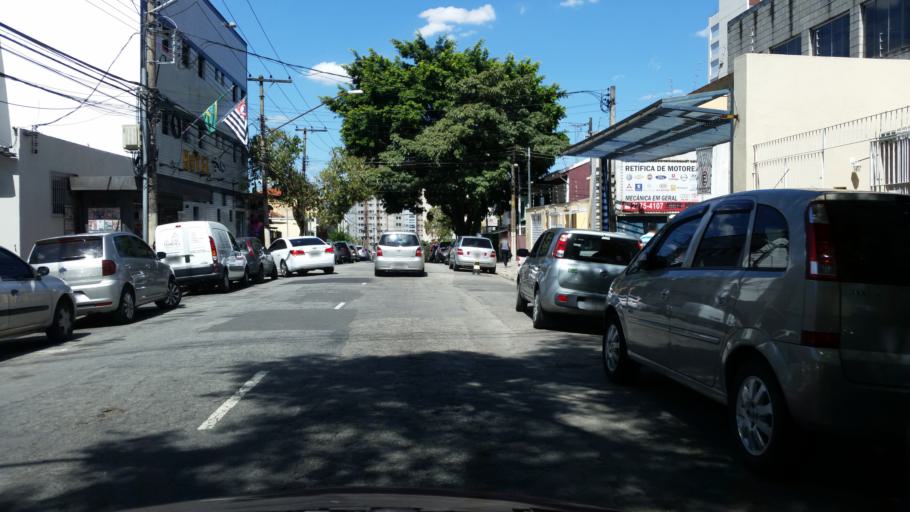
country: BR
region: Sao Paulo
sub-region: Diadema
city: Diadema
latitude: -23.6179
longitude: -46.6375
